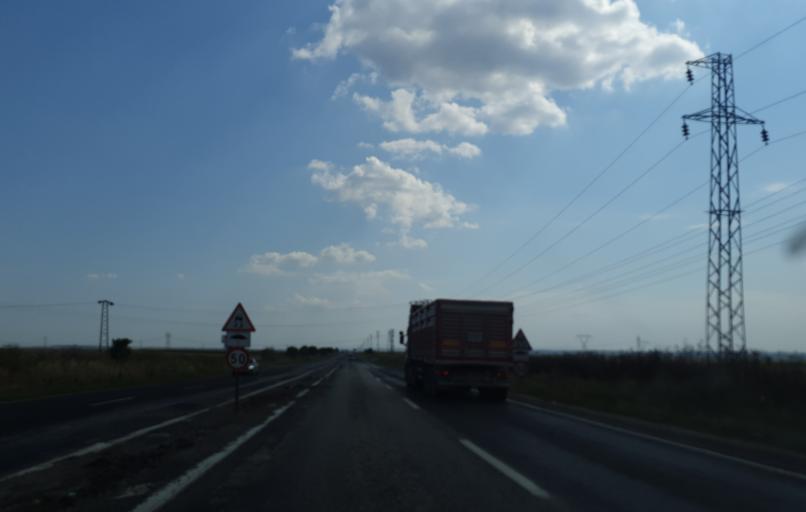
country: TR
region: Kirklareli
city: Buyukkaristiran
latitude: 41.2431
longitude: 27.5387
